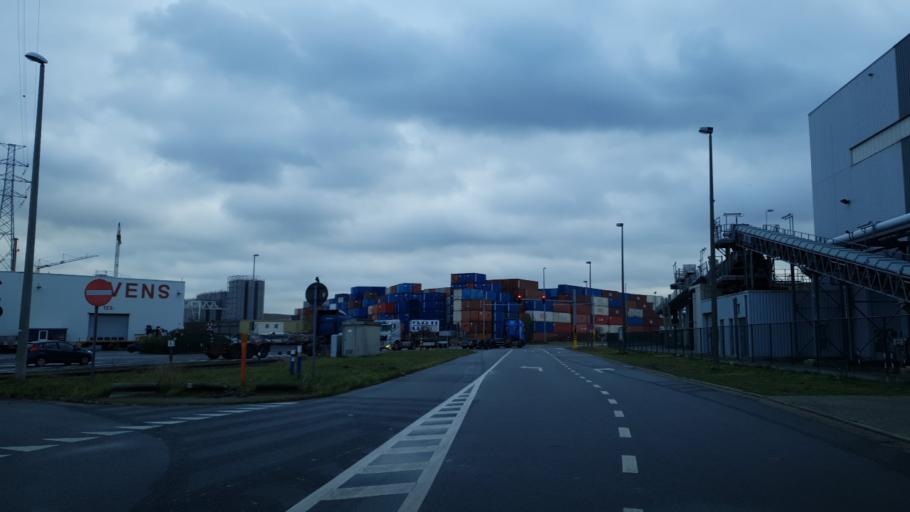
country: BE
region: Flanders
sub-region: Provincie Antwerpen
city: Stabroek
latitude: 51.3081
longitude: 4.3267
